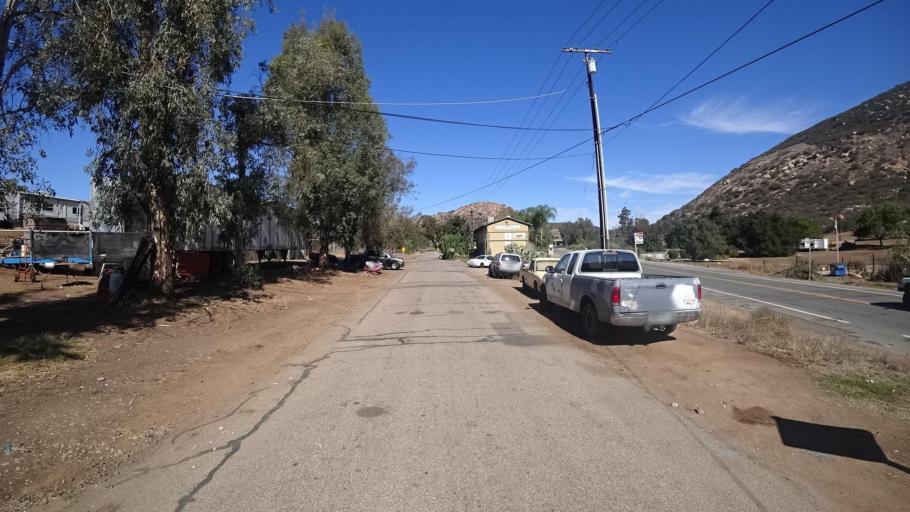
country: US
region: California
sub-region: San Diego County
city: Harbison Canyon
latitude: 32.8505
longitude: -116.8584
